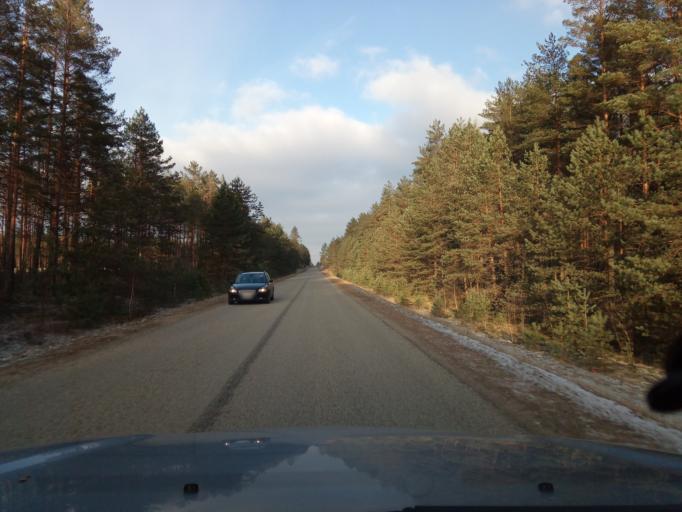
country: LT
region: Alytaus apskritis
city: Varena
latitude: 54.1709
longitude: 24.5088
